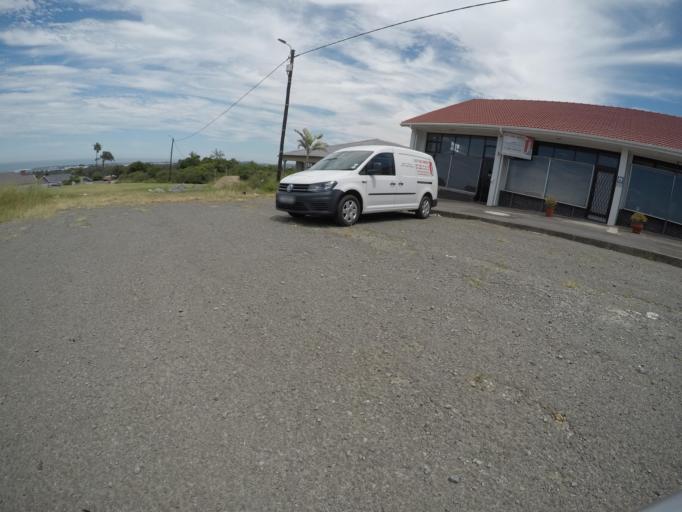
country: ZA
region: Eastern Cape
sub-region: Buffalo City Metropolitan Municipality
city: East London
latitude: -33.0402
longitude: 27.8555
